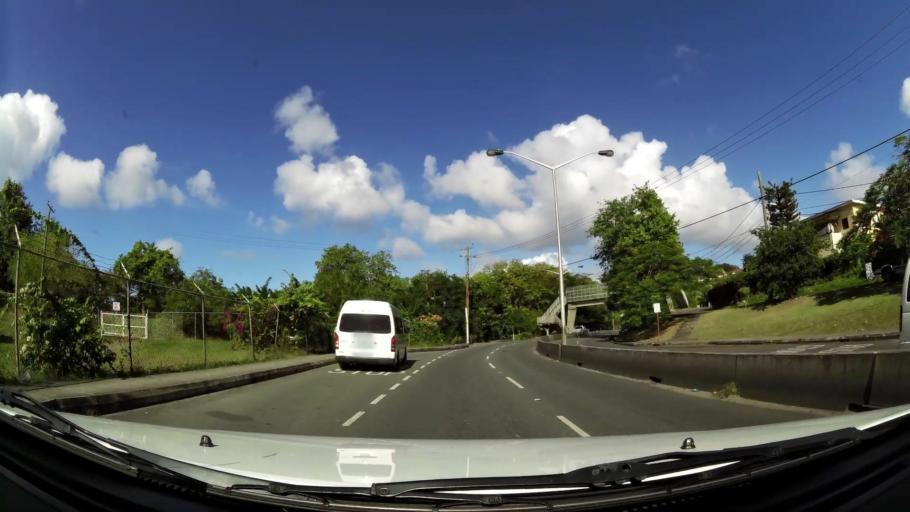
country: LC
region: Castries Quarter
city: Bisee
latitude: 14.0295
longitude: -60.9781
